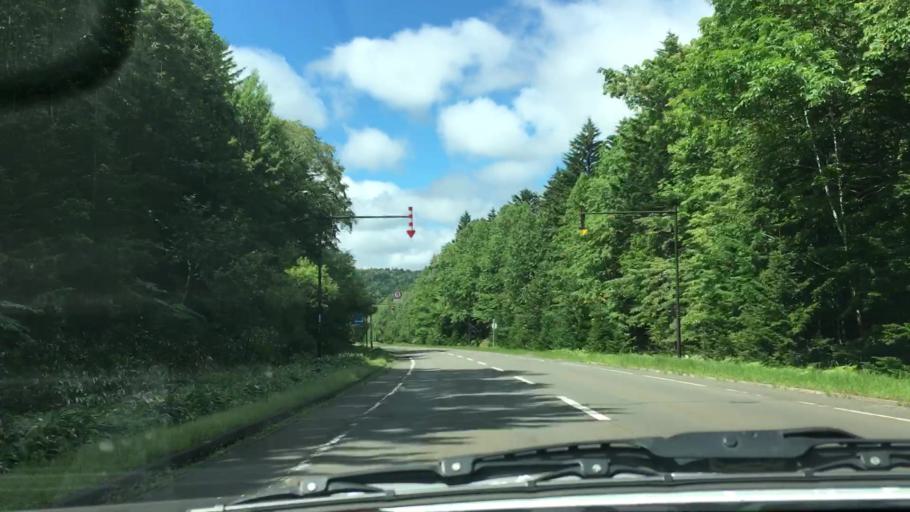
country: JP
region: Hokkaido
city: Kitami
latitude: 43.4477
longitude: 144.0282
